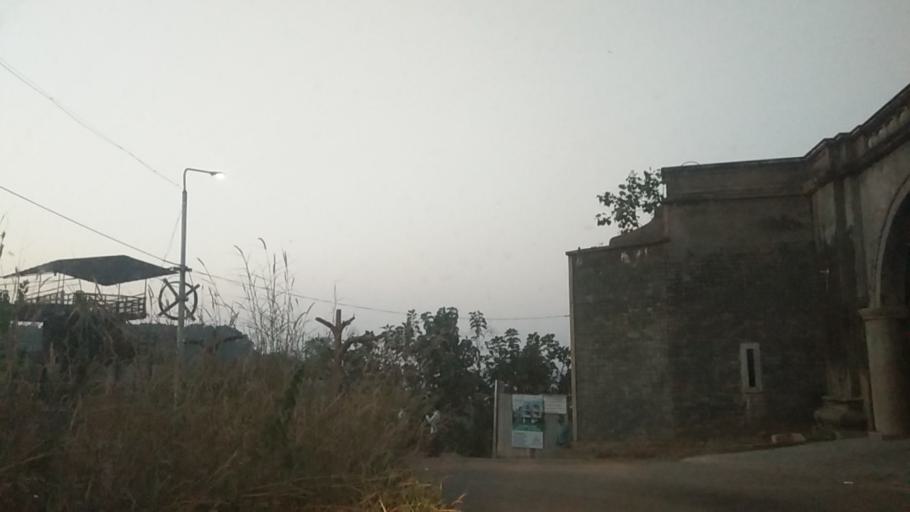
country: IN
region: Goa
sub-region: South Goa
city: Madgaon
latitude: 15.2775
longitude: 73.9702
